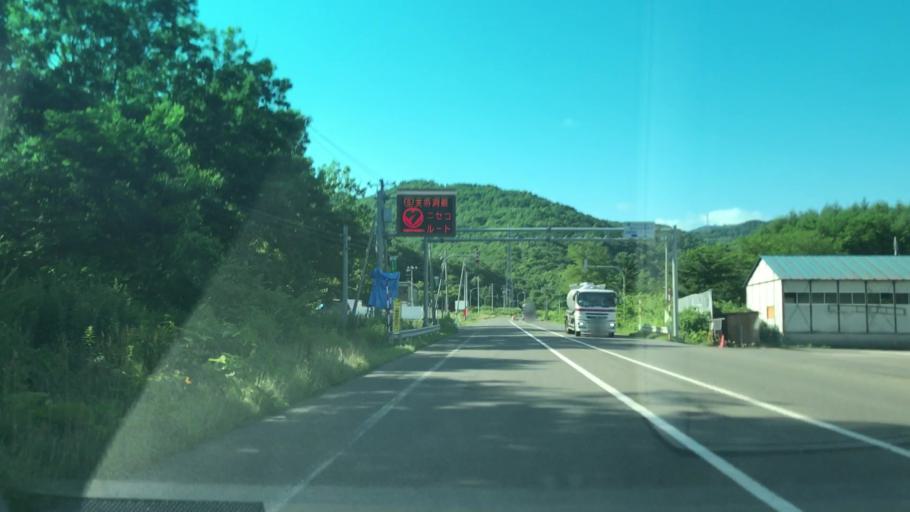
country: JP
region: Hokkaido
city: Iwanai
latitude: 43.0055
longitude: 140.6668
